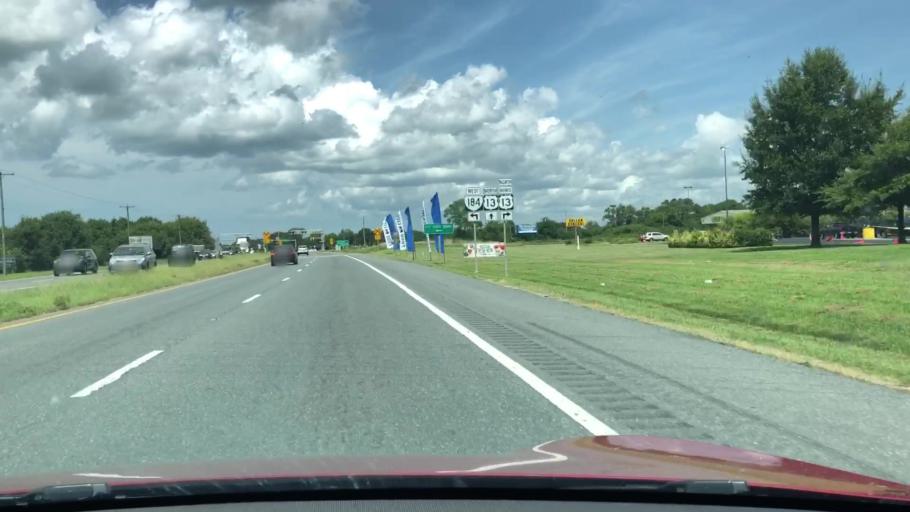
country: US
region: Virginia
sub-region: Northampton County
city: Cape Charles
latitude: 37.2690
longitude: -75.9746
